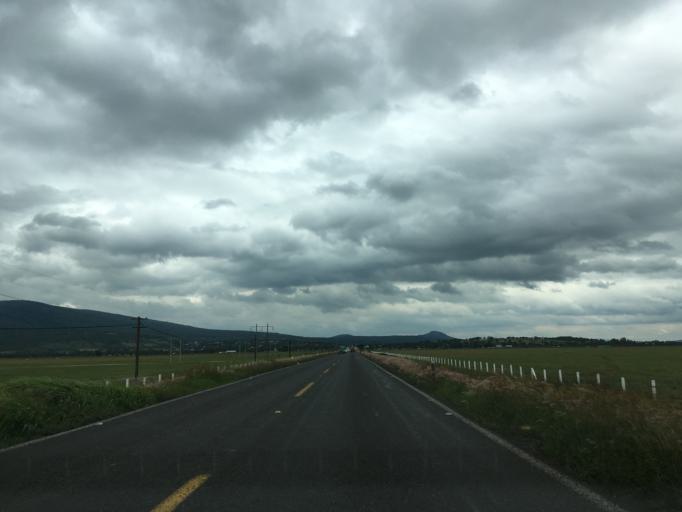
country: MX
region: Michoacan
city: Cuitzeo del Porvenir
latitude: 19.9780
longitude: -101.1425
